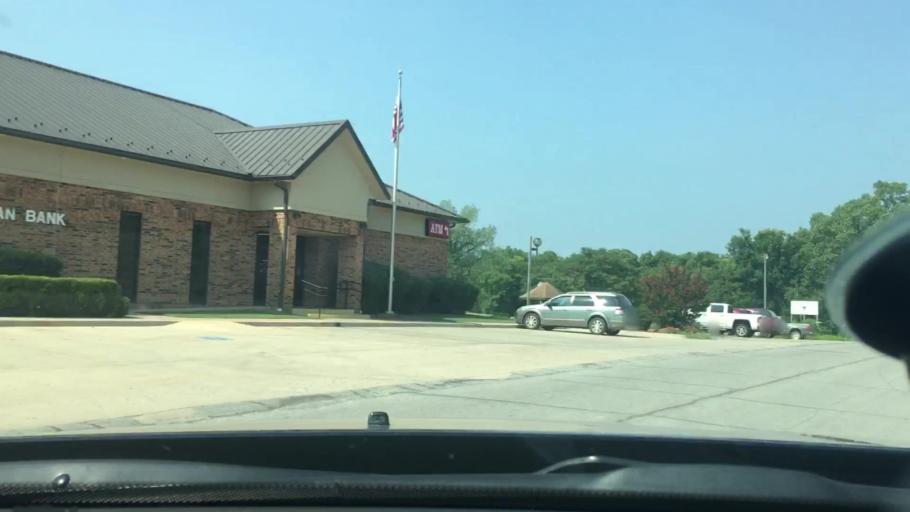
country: US
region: Oklahoma
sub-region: Pontotoc County
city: Ada
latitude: 34.6528
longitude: -96.5287
